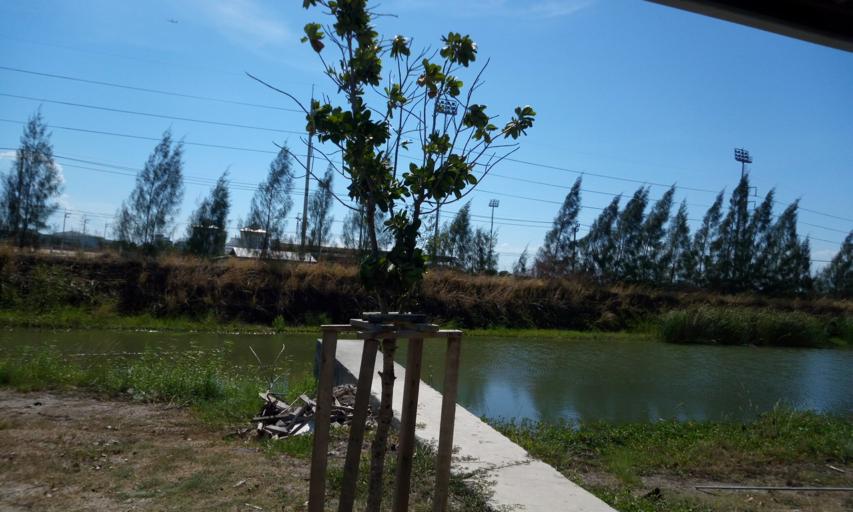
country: TH
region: Samut Prakan
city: Bang Bo District
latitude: 13.5258
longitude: 100.7595
